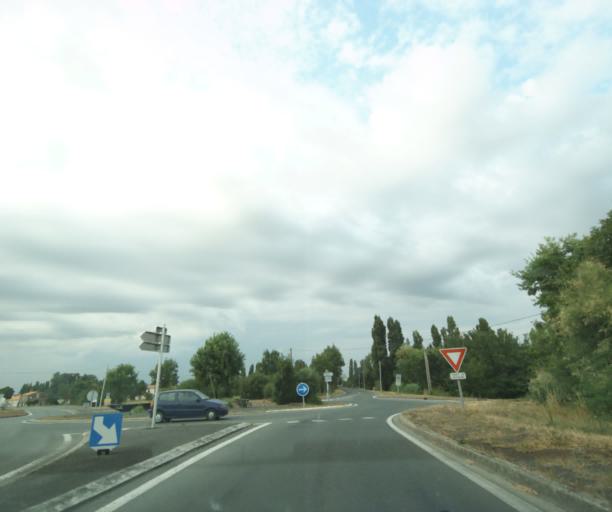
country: FR
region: Pays de la Loire
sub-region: Departement de la Vendee
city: Chaille-les-Marais
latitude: 46.3635
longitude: -0.9885
